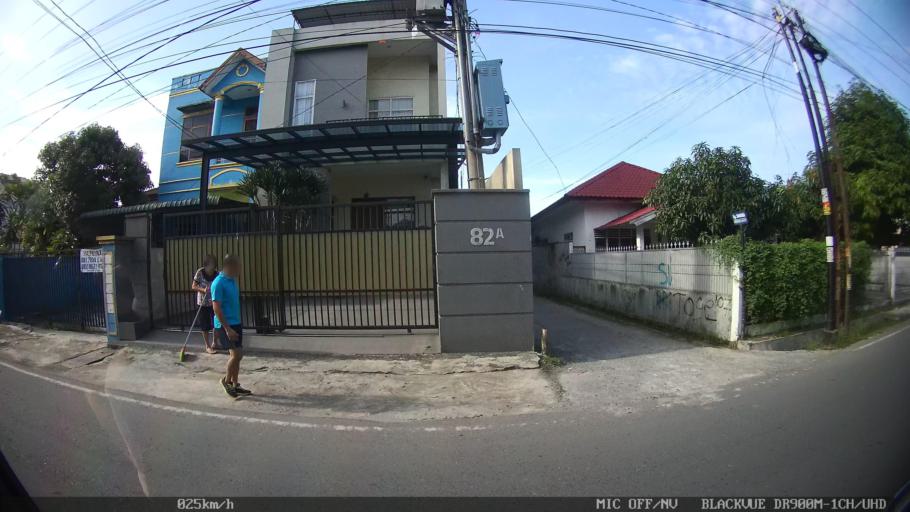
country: ID
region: North Sumatra
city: Medan
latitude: 3.6041
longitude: 98.6511
